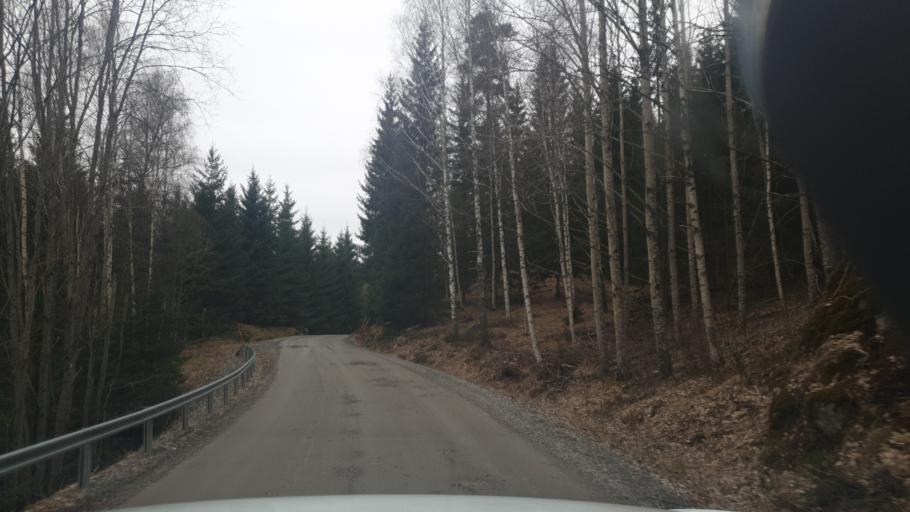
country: NO
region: Ostfold
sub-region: Romskog
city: Romskog
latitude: 59.6930
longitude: 11.9438
